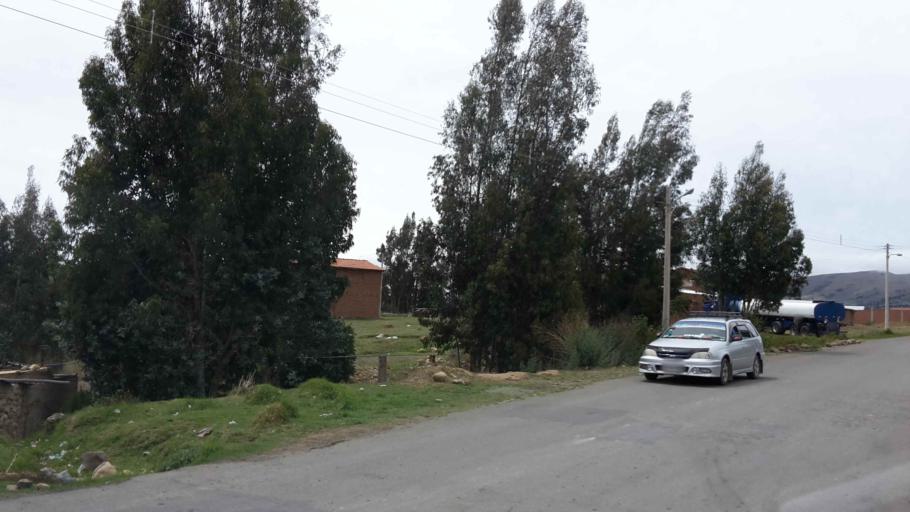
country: BO
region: Cochabamba
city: Arani
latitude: -17.4556
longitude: -65.7186
